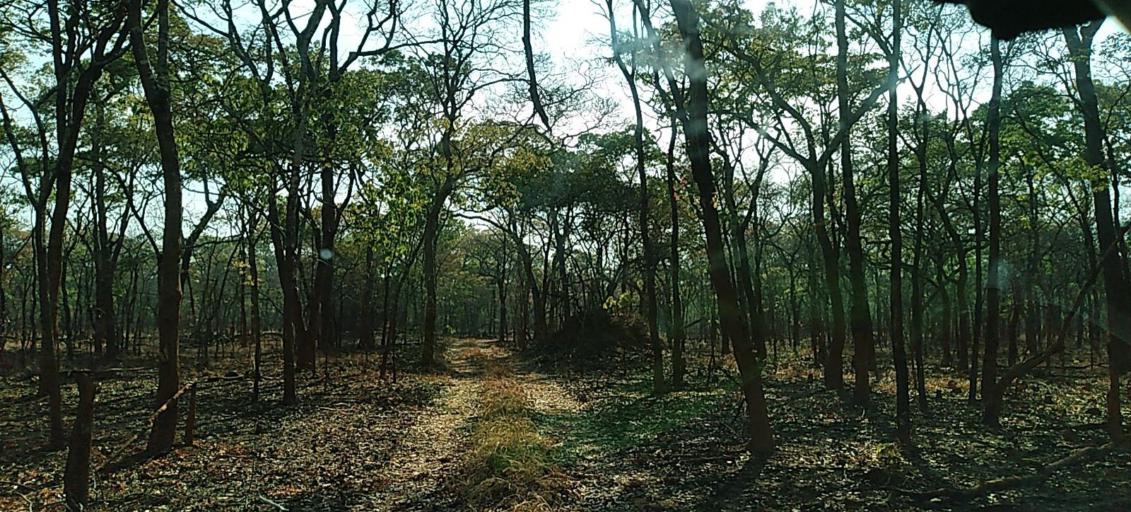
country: ZM
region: North-Western
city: Kalengwa
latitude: -13.2273
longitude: 25.0908
